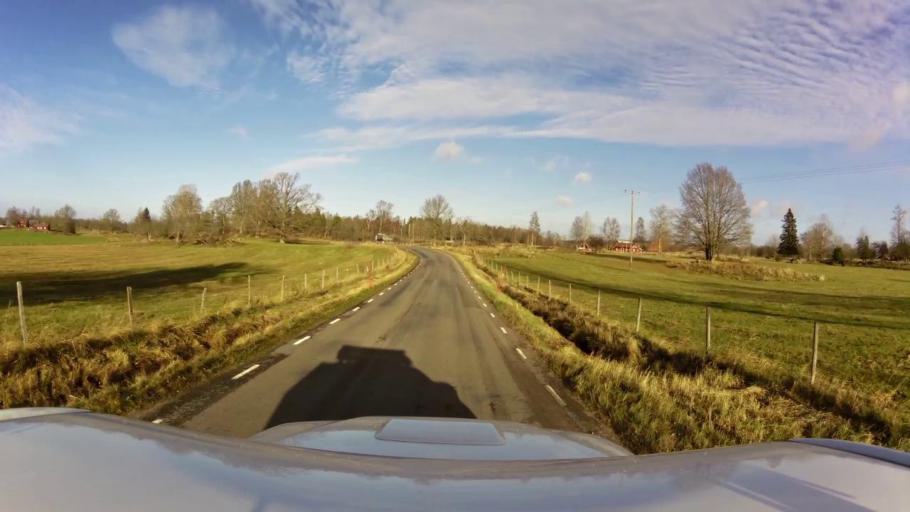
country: SE
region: OEstergoetland
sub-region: Linkopings Kommun
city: Linkoping
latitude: 58.3379
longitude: 15.6525
